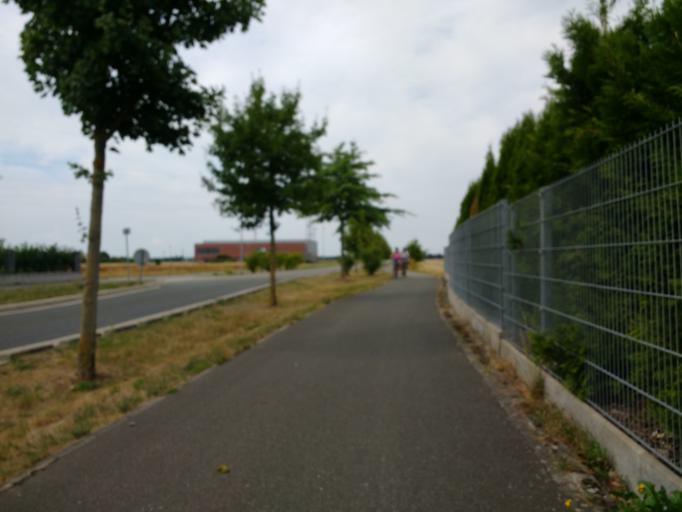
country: DE
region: Lower Saxony
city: Gifhorn
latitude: 52.4989
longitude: 10.5318
